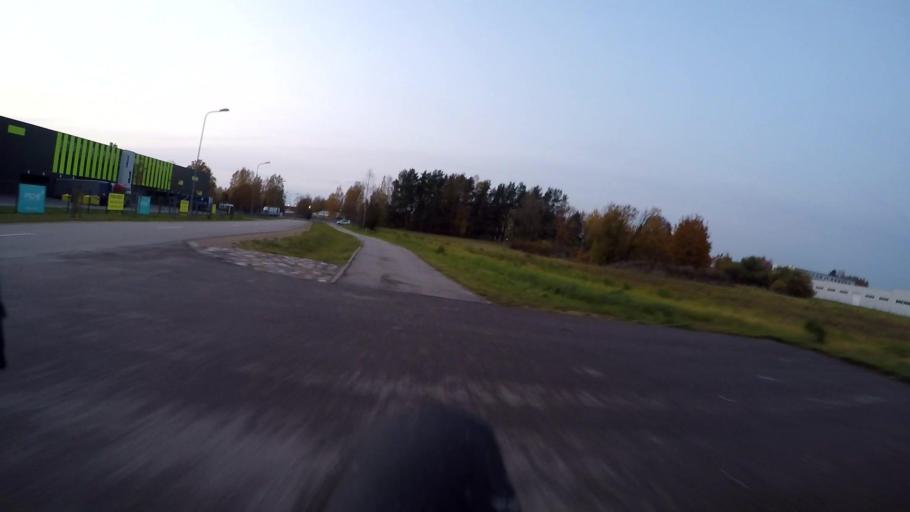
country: LV
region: Marupe
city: Marupe
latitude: 56.9176
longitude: 23.9905
